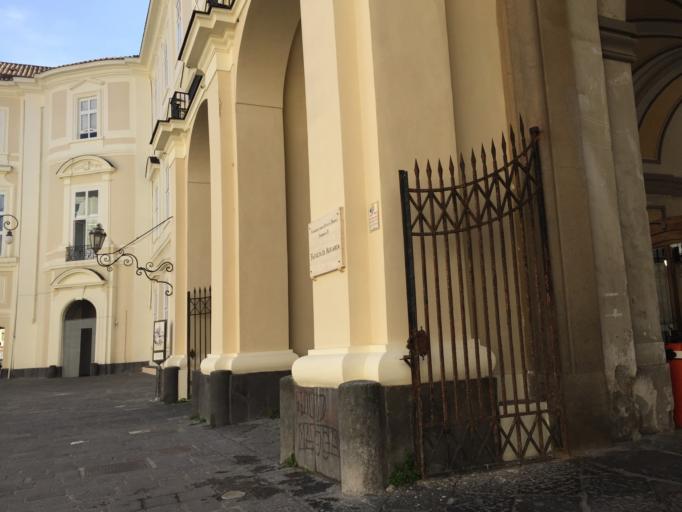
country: IT
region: Campania
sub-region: Provincia di Napoli
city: Portici
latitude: 40.8114
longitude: 14.3427
